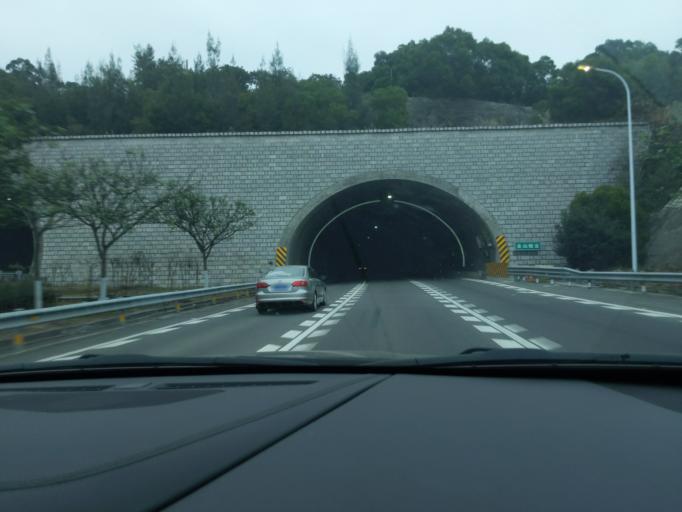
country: CN
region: Fujian
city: Shishi
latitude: 24.7505
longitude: 118.5995
